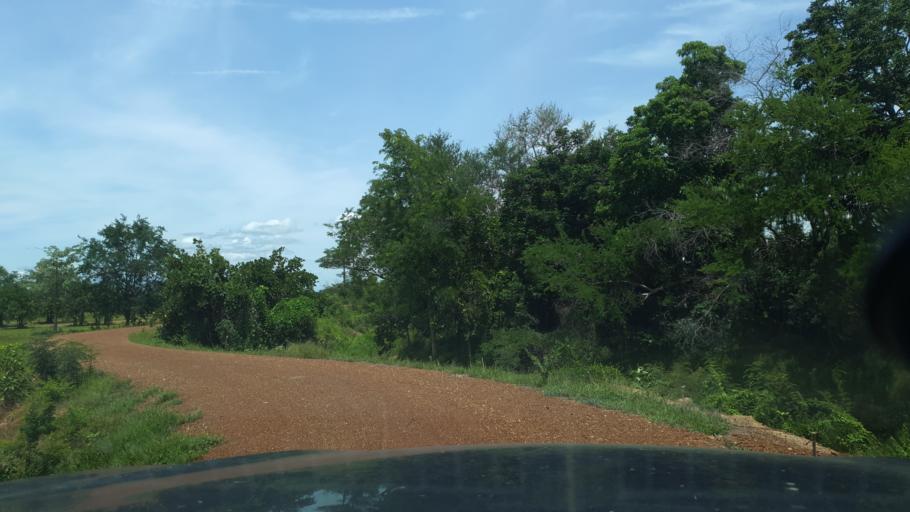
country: TH
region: Sukhothai
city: Ban Na
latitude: 17.0803
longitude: 99.6922
